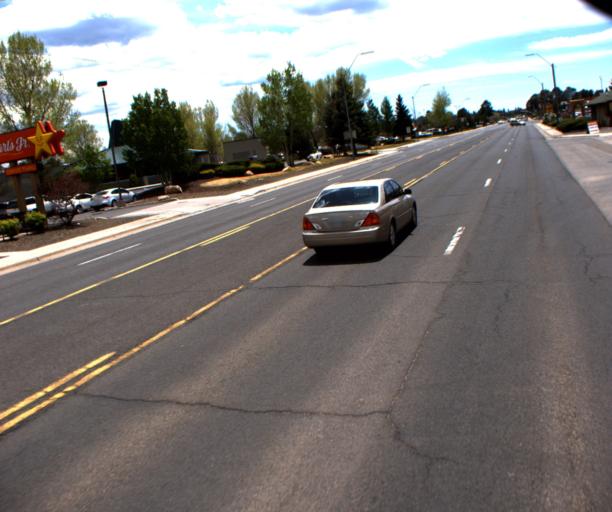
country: US
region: Arizona
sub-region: Coconino County
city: Flagstaff
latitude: 35.1872
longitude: -111.6616
